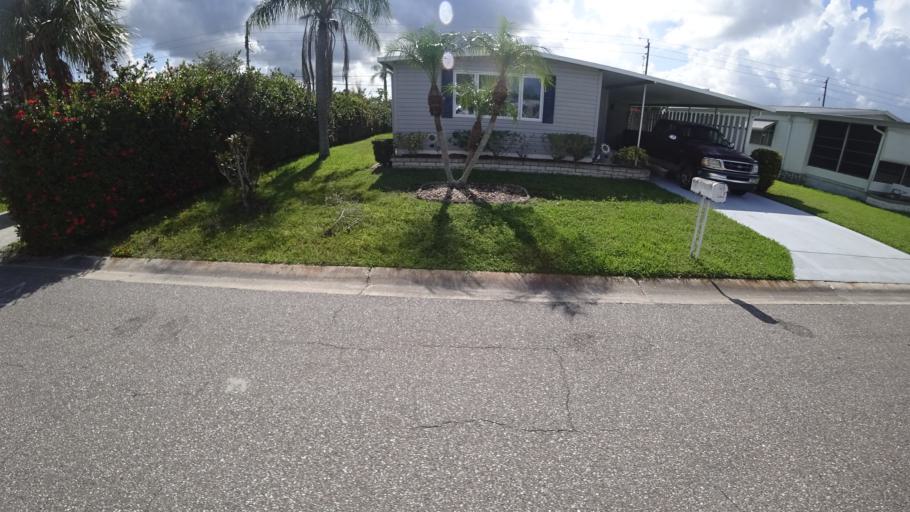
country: US
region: Florida
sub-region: Manatee County
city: West Samoset
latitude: 27.4490
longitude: -82.5602
